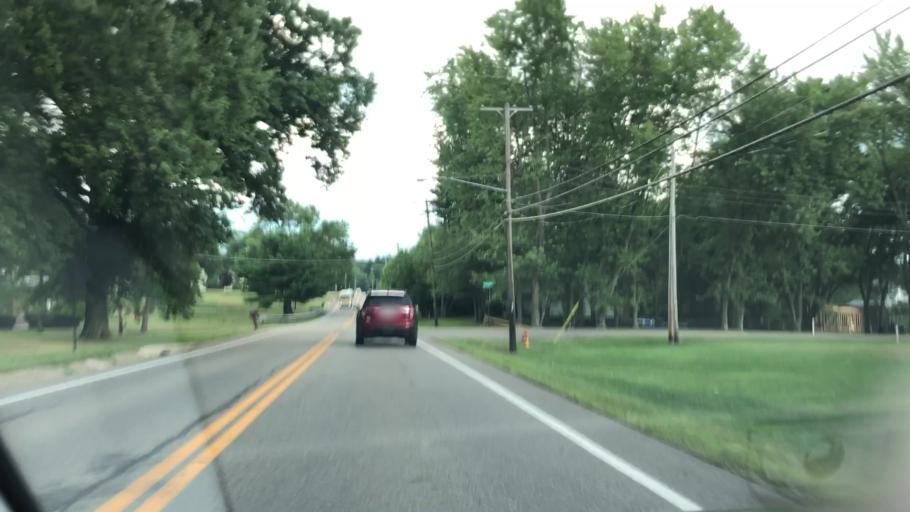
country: US
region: Ohio
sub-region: Summit County
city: Green
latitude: 40.9448
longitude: -81.4888
